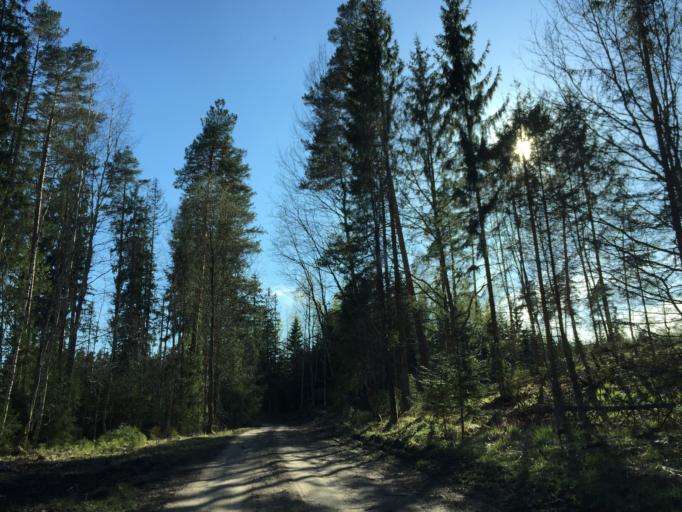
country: EE
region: Valgamaa
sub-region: Valga linn
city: Valga
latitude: 57.7751
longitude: 26.2280
